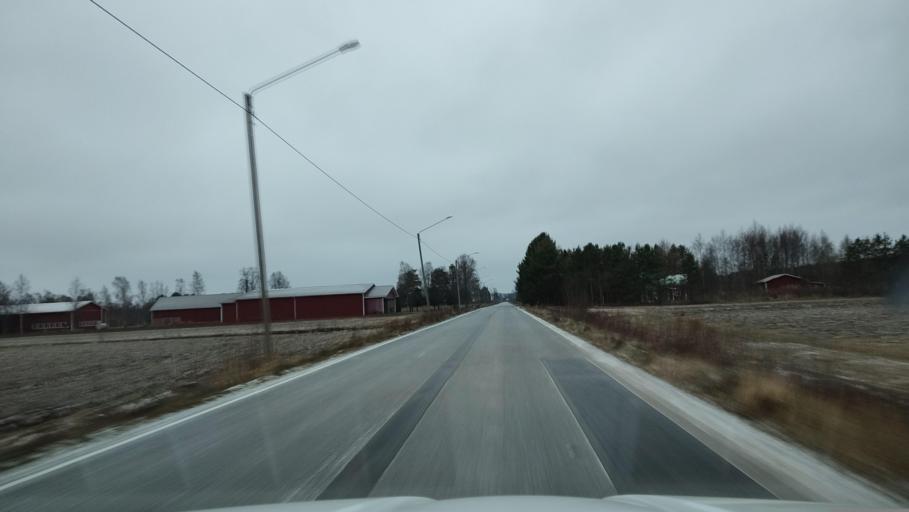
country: FI
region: Southern Ostrobothnia
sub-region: Suupohja
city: Karijoki
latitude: 62.2431
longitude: 21.6667
